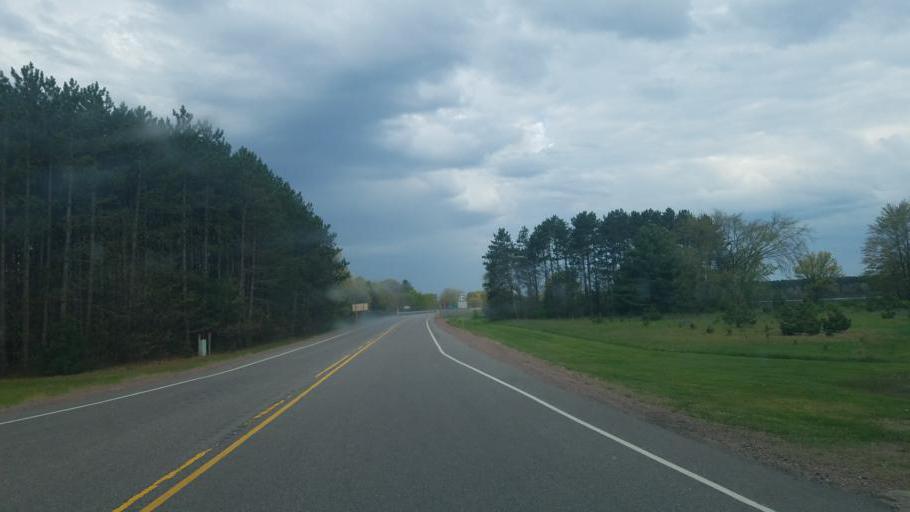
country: US
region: Wisconsin
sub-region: Wood County
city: Nekoosa
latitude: 44.3777
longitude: -90.1115
